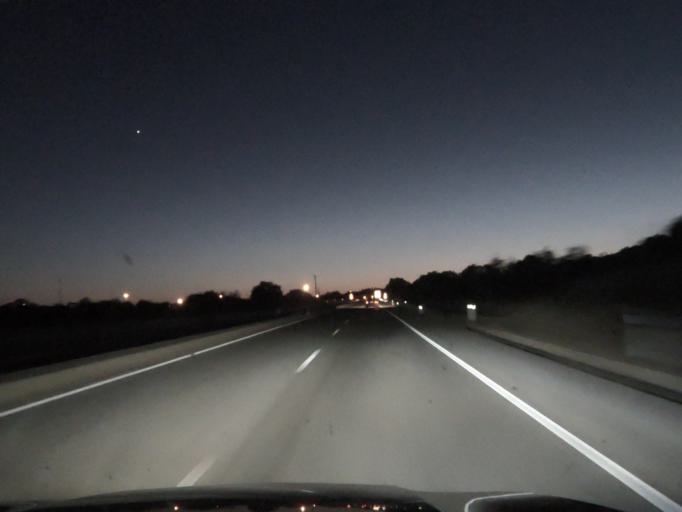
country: PT
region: Faro
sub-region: Loule
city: Loule
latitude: 37.1450
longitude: -8.0358
